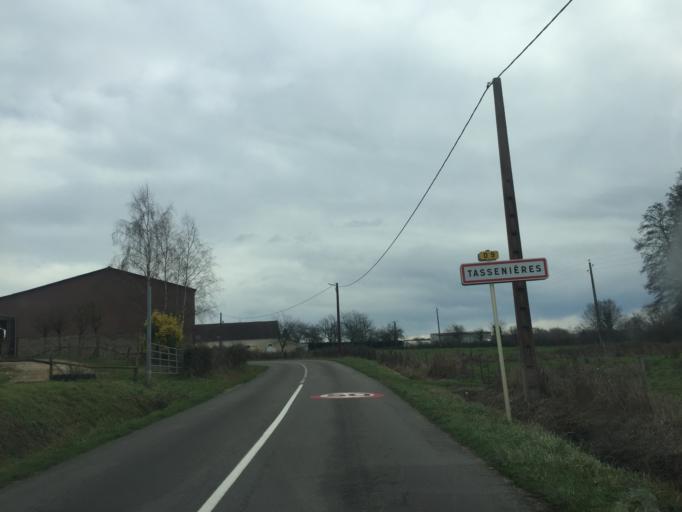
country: FR
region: Franche-Comte
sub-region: Departement du Jura
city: Mont-sous-Vaudrey
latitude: 46.9215
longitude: 5.5111
